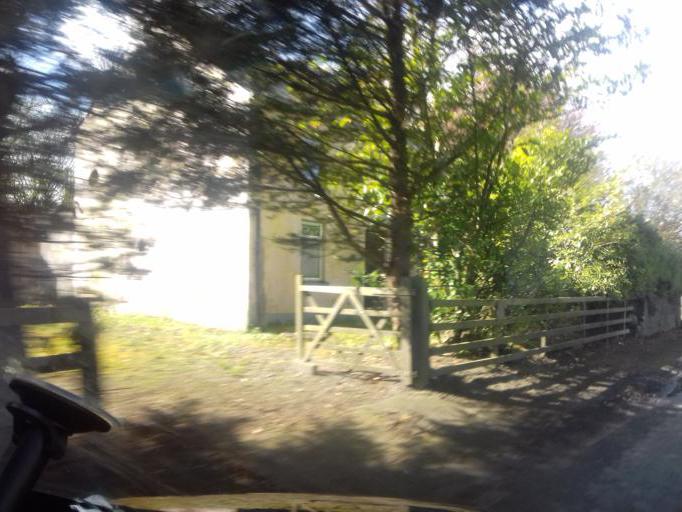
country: IE
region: Leinster
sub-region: An Mhi
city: Kells
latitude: 53.7197
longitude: -6.8878
